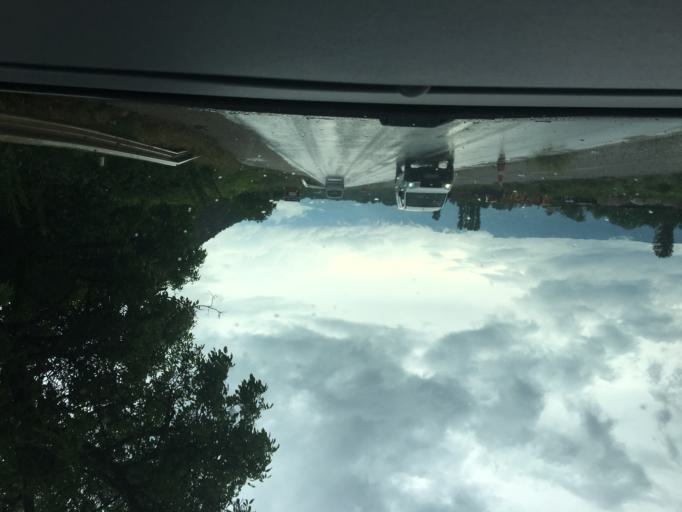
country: MK
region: Ohrid
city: Ohrid
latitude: 41.1371
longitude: 20.7701
